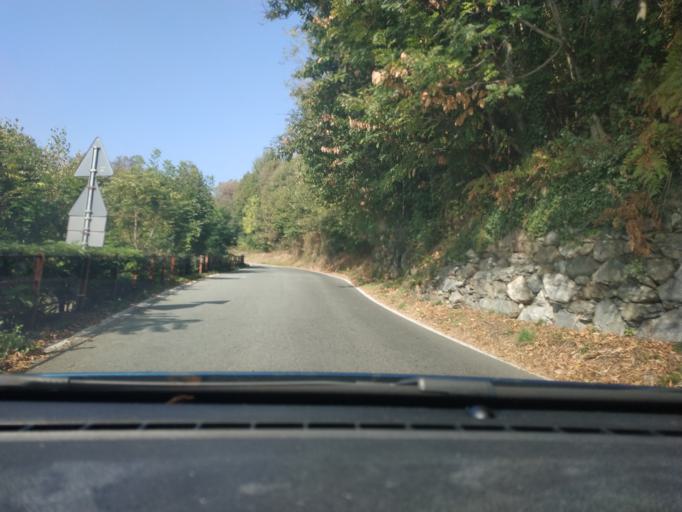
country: IT
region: Piedmont
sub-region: Provincia di Torino
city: Chiaverano
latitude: 45.5078
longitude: 7.9066
